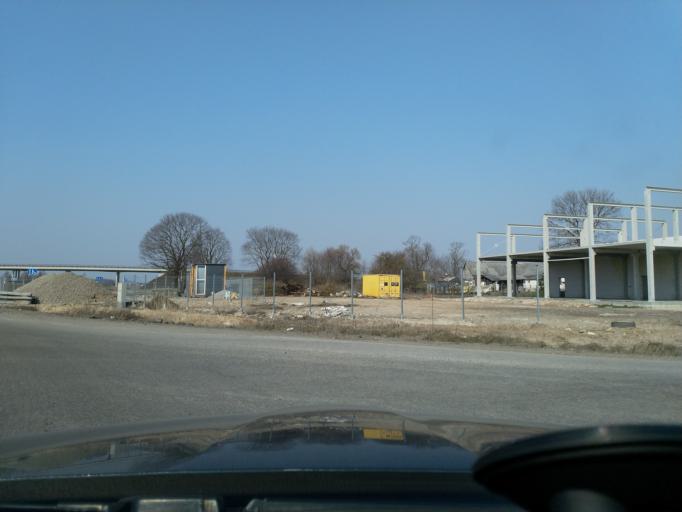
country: LT
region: Klaipedos apskritis
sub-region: Klaipeda
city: Klaipeda
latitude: 55.7524
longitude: 21.1721
